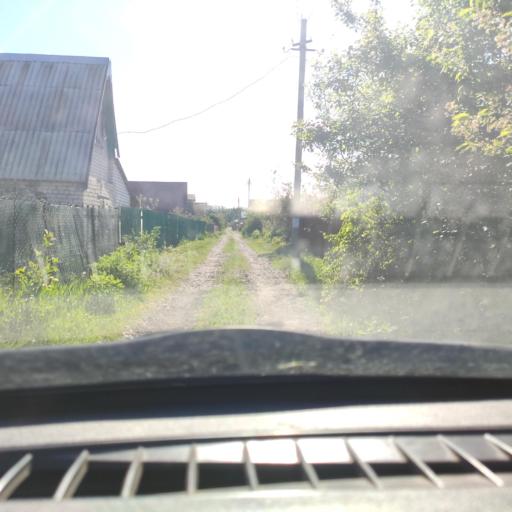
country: RU
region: Samara
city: Tol'yatti
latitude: 53.6271
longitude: 49.4068
